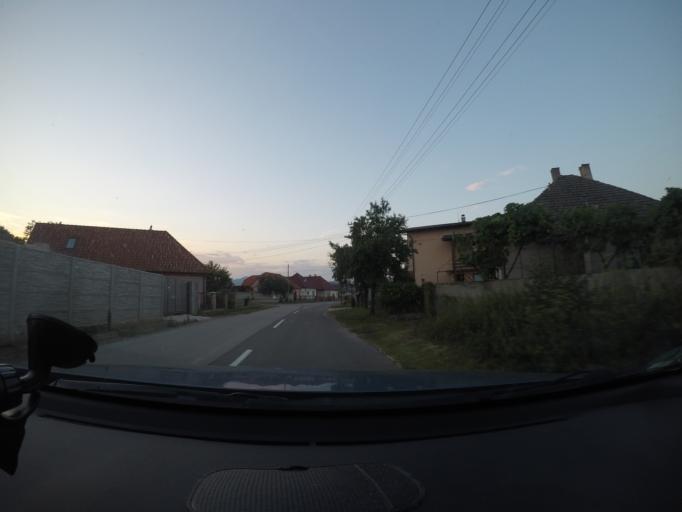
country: SK
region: Trenciansky
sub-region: Okres Nove Mesto nad Vahom
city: Nove Mesto nad Vahom
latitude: 48.8278
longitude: 17.9014
